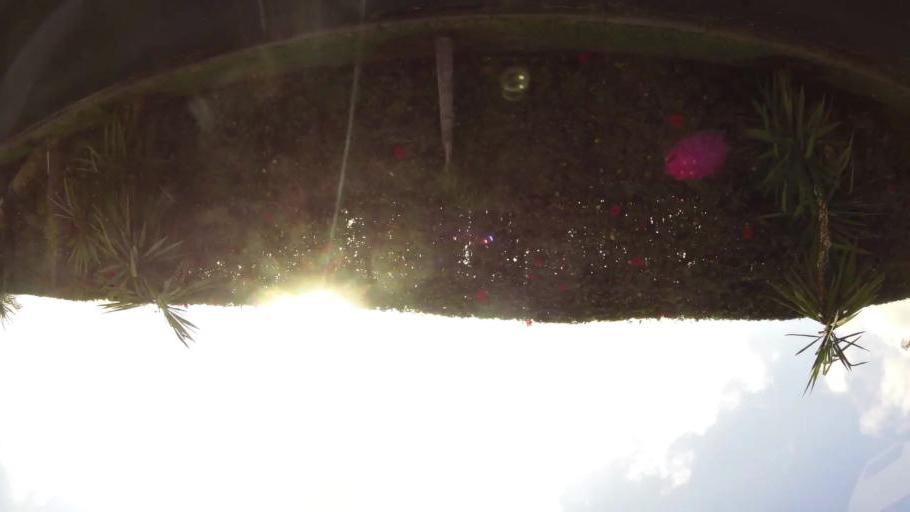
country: MA
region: Rabat-Sale-Zemmour-Zaer
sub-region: Rabat
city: Rabat
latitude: 33.9615
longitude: -6.8464
